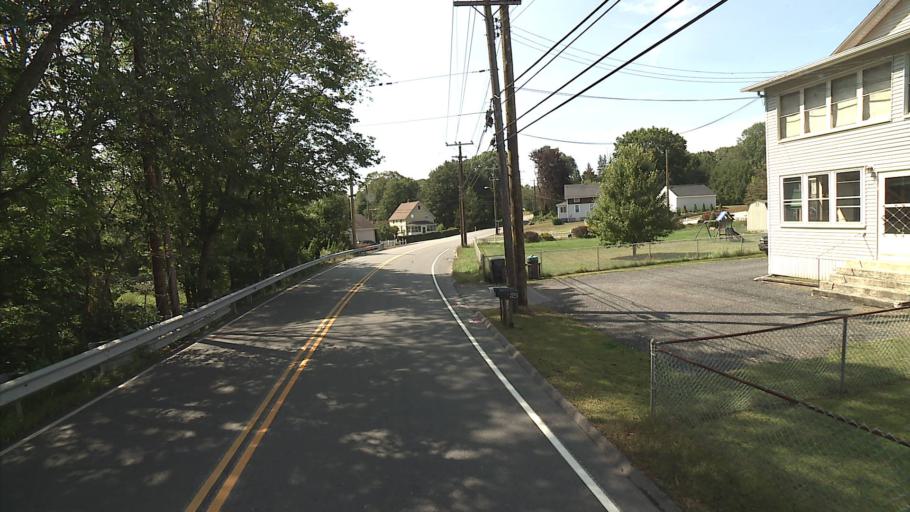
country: US
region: Connecticut
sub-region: New London County
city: Lisbon
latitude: 41.5711
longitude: -72.0334
